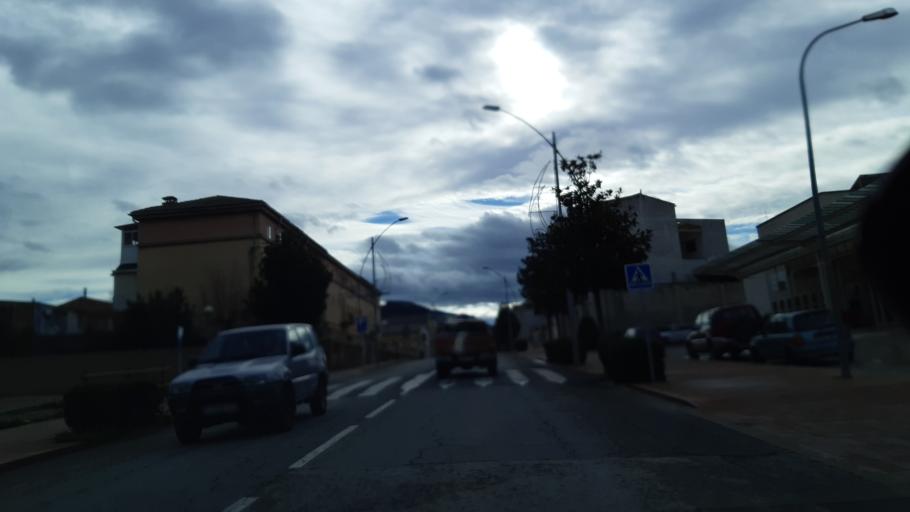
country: ES
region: Catalonia
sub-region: Provincia de Tarragona
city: Gandesa
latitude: 41.0578
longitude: 0.4413
